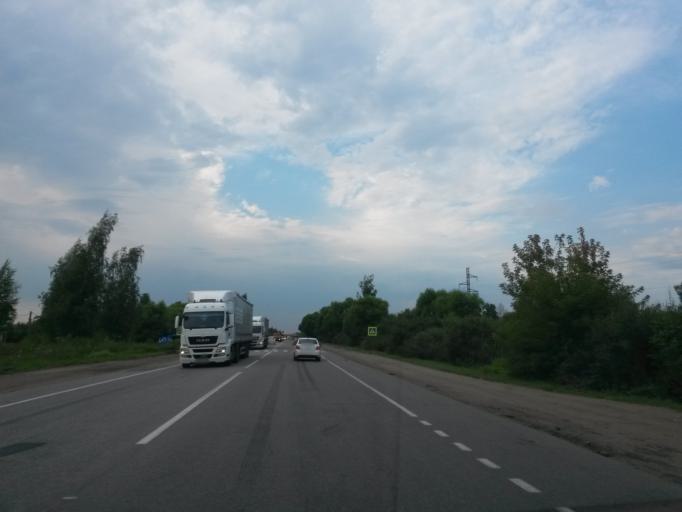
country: RU
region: Jaroslavl
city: Yaroslavl
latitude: 57.6046
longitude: 39.7941
